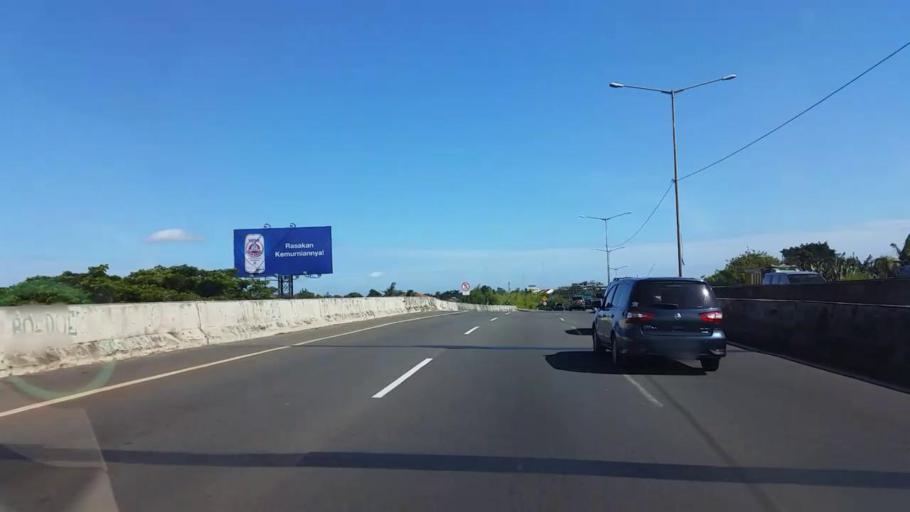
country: ID
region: Banten
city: South Tangerang
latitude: -6.2564
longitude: 106.7606
